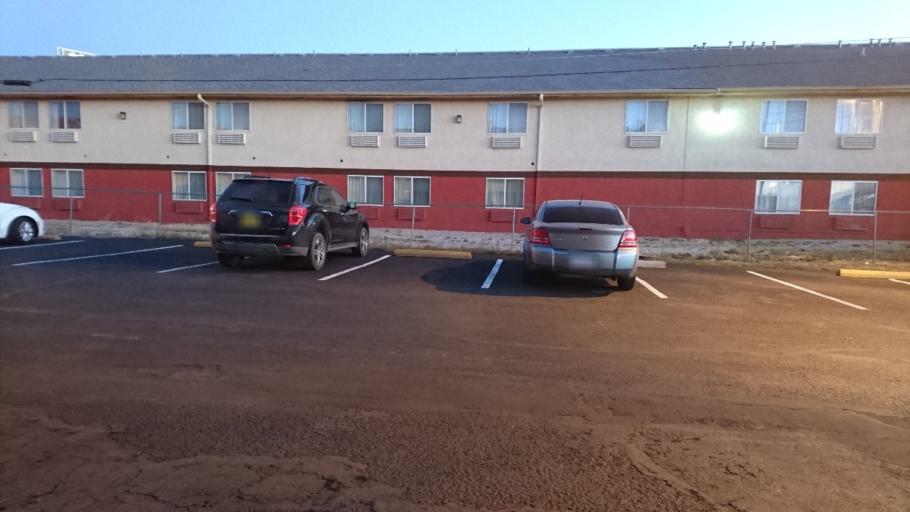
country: US
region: New Mexico
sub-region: Cibola County
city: Grants
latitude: 35.1269
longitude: -107.8270
